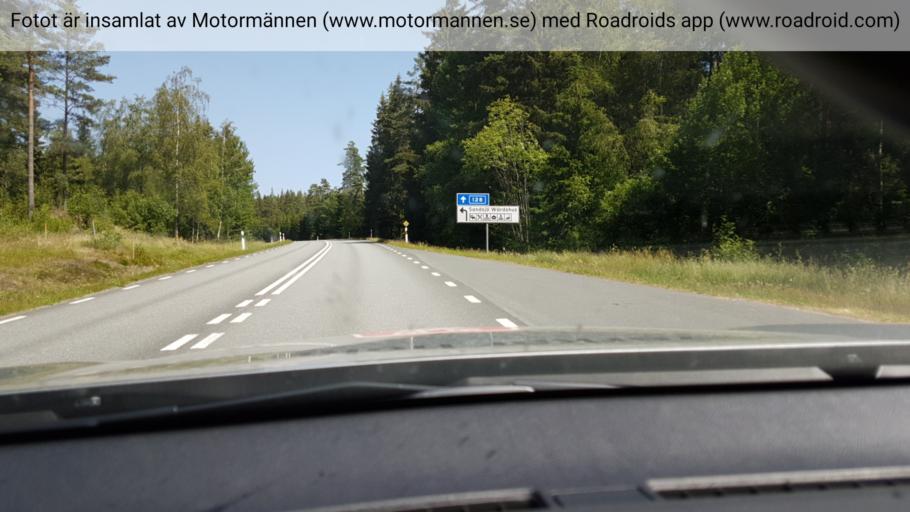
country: SE
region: Joenkoeping
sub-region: Nassjo Kommun
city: Bodafors
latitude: 57.4762
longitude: 14.7805
